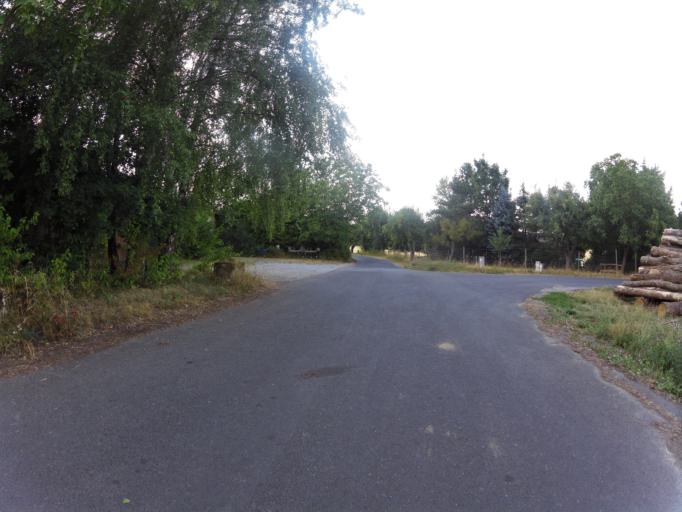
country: DE
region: Bavaria
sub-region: Regierungsbezirk Unterfranken
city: Ochsenfurt
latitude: 49.6500
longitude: 10.0704
